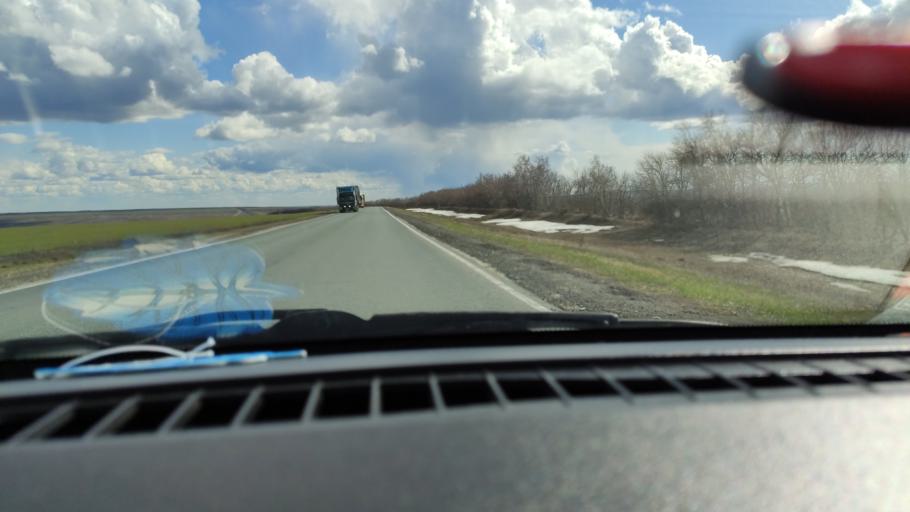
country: RU
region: Saratov
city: Dukhovnitskoye
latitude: 52.7668
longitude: 48.2377
